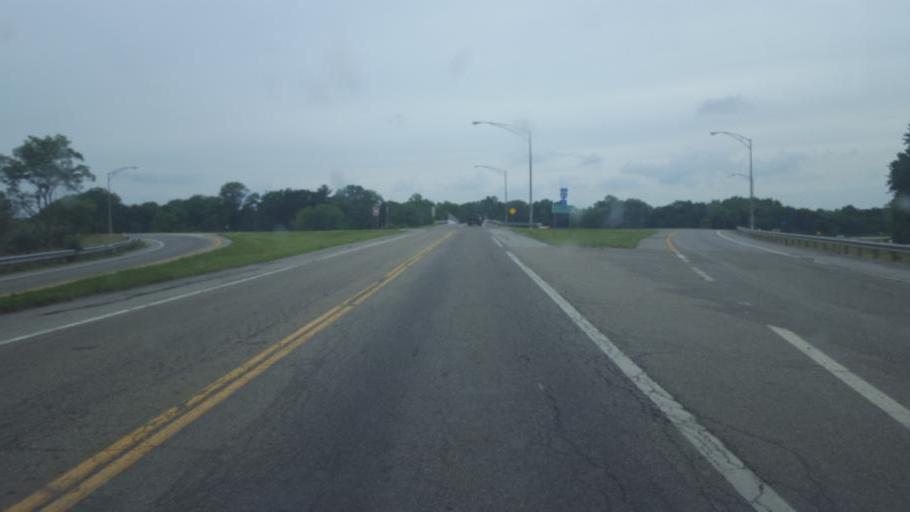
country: US
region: Ohio
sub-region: Trumbull County
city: Leavittsburg
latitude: 41.2398
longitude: -80.8860
